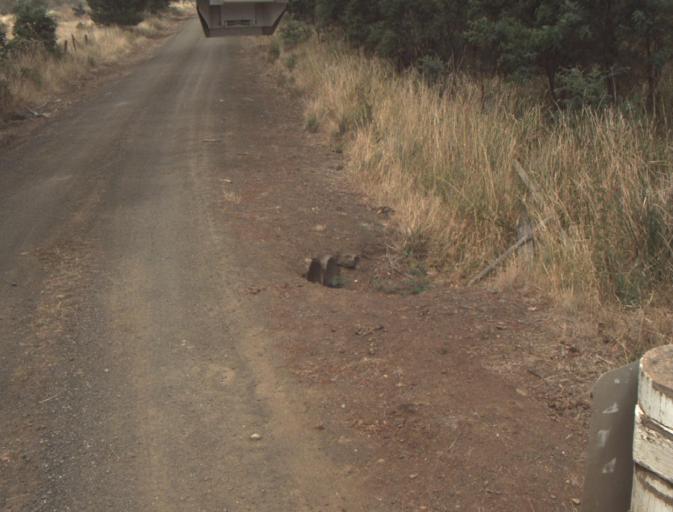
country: AU
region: Tasmania
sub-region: Northern Midlands
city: Evandale
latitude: -41.5040
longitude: 147.3576
